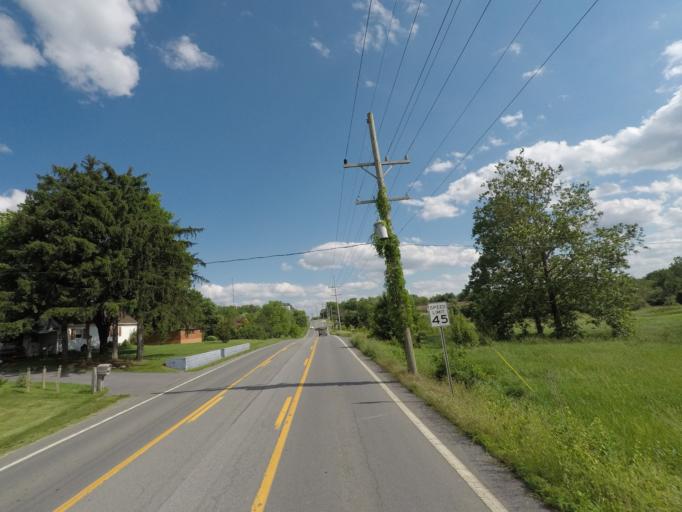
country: US
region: West Virginia
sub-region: Berkeley County
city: Martinsburg
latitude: 39.4168
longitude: -77.9188
